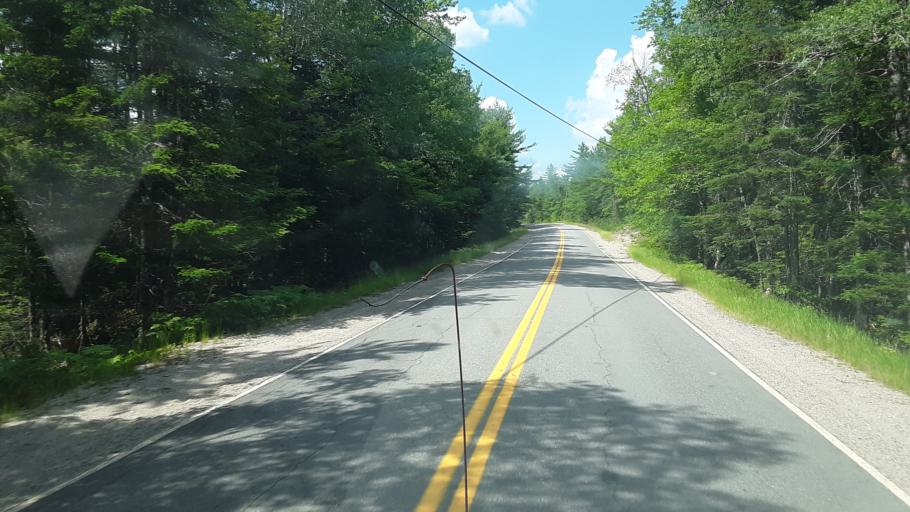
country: US
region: Maine
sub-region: Washington County
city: Machias
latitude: 44.8841
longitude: -67.6220
